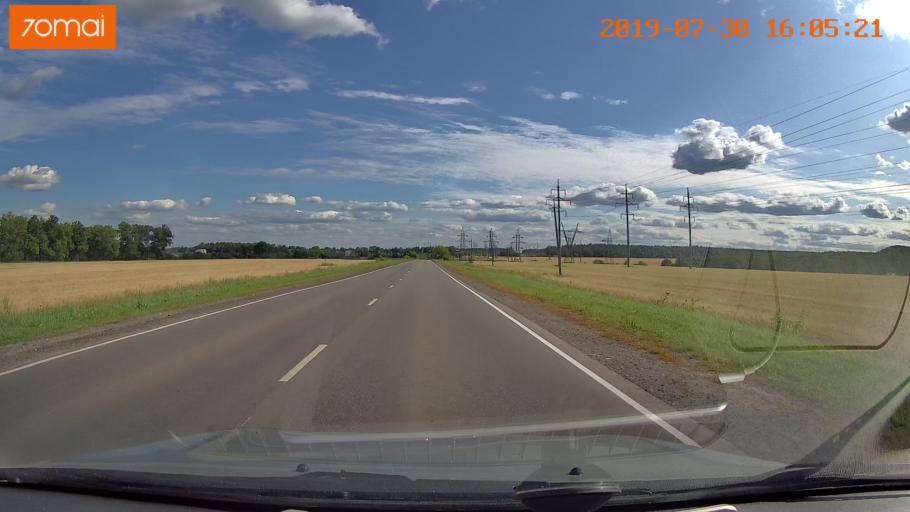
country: RU
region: Moskovskaya
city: Peski
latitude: 55.2668
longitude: 38.7147
